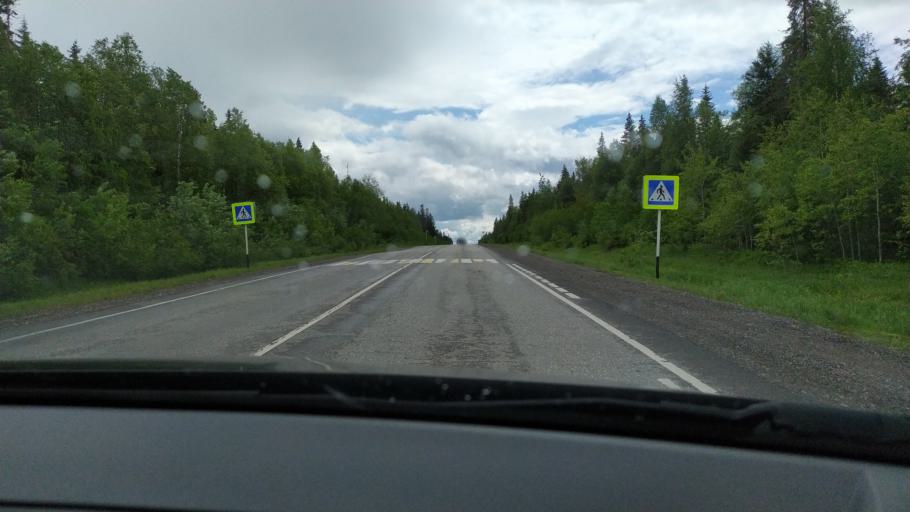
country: RU
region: Perm
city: Gremyachinsk
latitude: 58.5106
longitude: 57.8117
